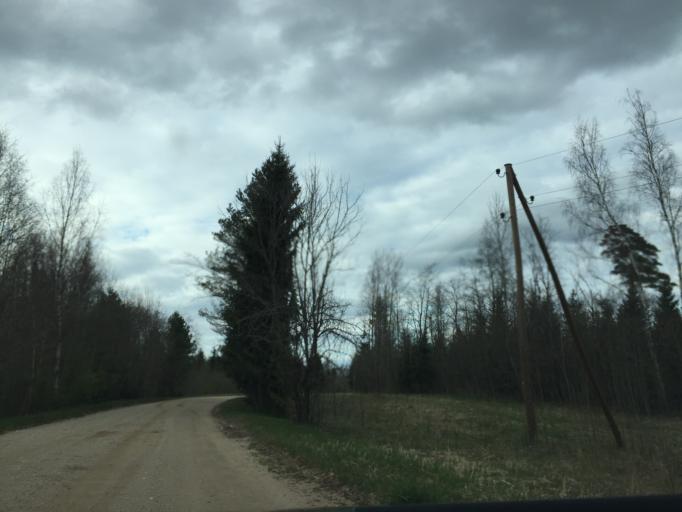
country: LV
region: Aluksnes Rajons
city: Aluksne
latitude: 57.4079
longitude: 27.0021
